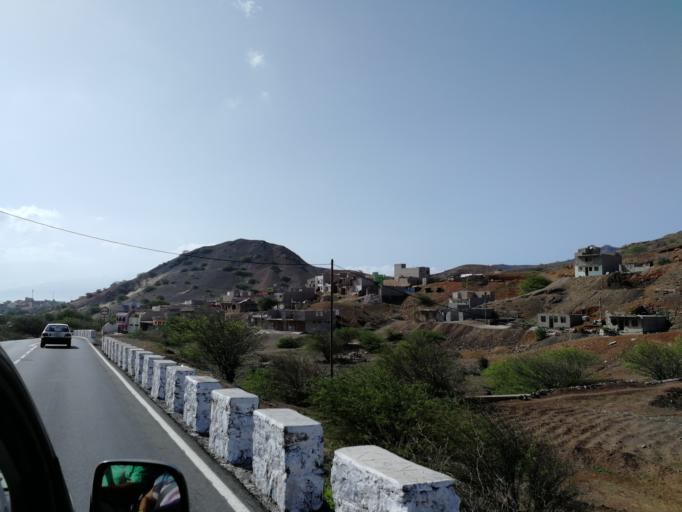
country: CV
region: Sao Vicente
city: Mindelo
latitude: 16.8805
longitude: -24.9676
